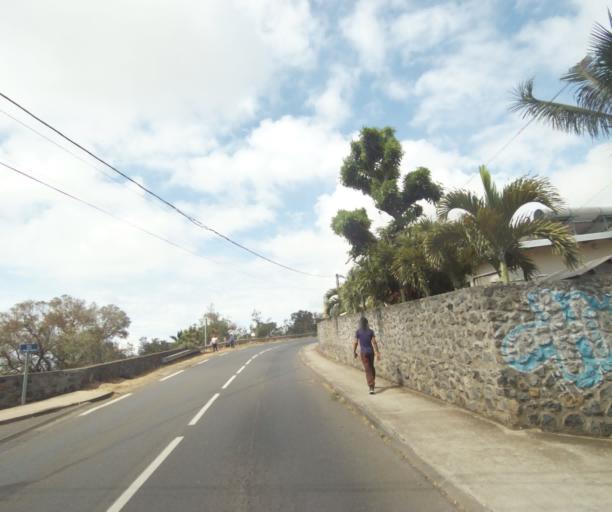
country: RE
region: Reunion
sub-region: Reunion
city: Saint-Paul
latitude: -21.0452
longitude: 55.2613
